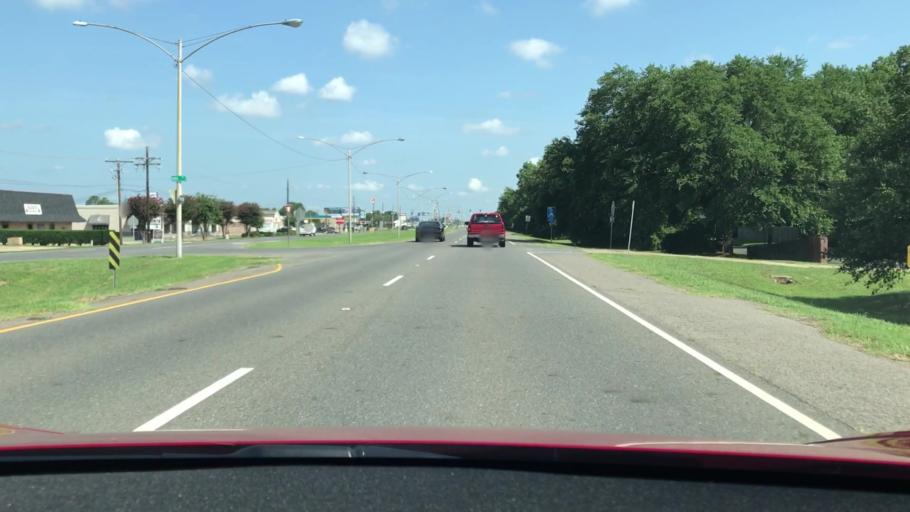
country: US
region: Louisiana
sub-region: Bossier Parish
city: Bossier City
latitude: 32.4180
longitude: -93.7037
